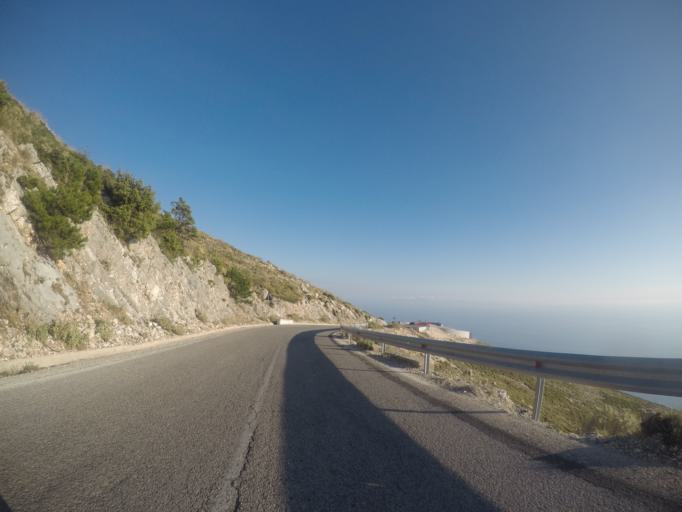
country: AL
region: Vlore
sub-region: Rrethi i Vlores
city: Vranisht
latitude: 40.1897
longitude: 19.5985
